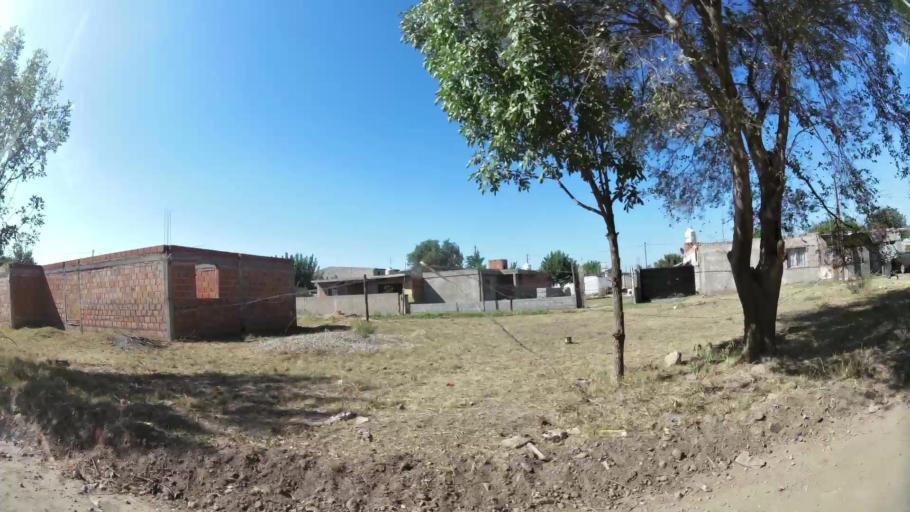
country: AR
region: Cordoba
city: Villa Allende
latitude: -31.3217
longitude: -64.2447
